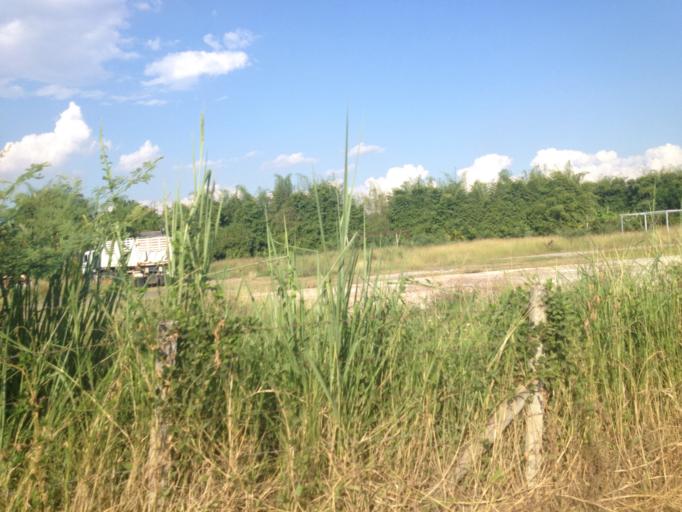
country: TH
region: Chiang Mai
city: Hang Dong
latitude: 18.7001
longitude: 98.9239
